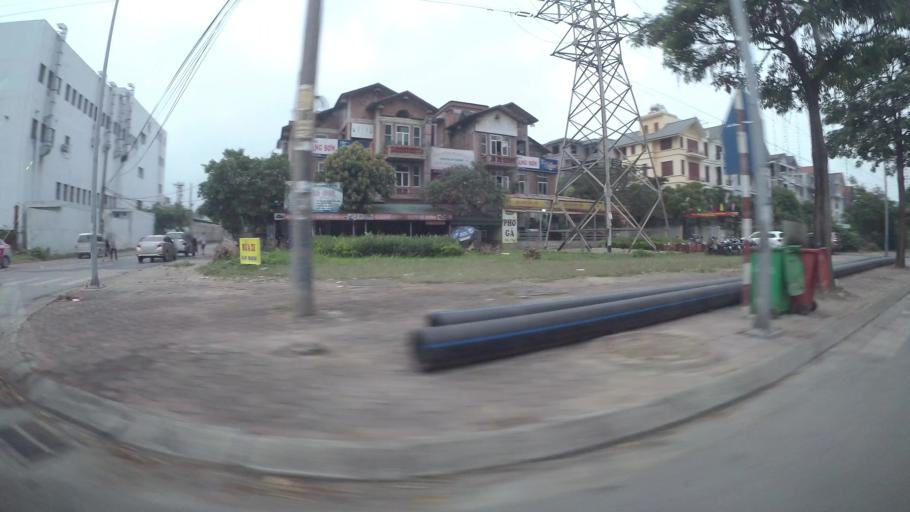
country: VN
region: Ha Noi
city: Trau Quy
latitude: 21.0352
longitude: 105.9057
